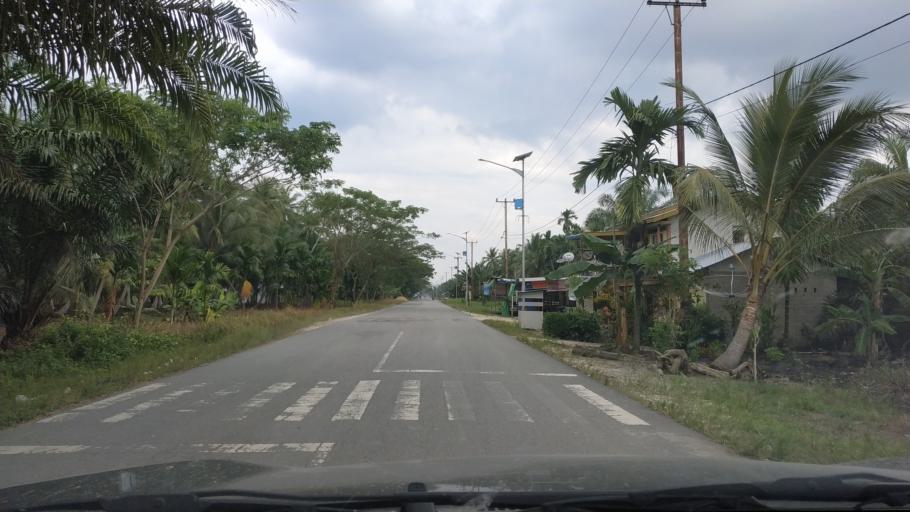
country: ID
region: Riau
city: Sungaisalak
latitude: -0.5665
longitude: 102.9713
